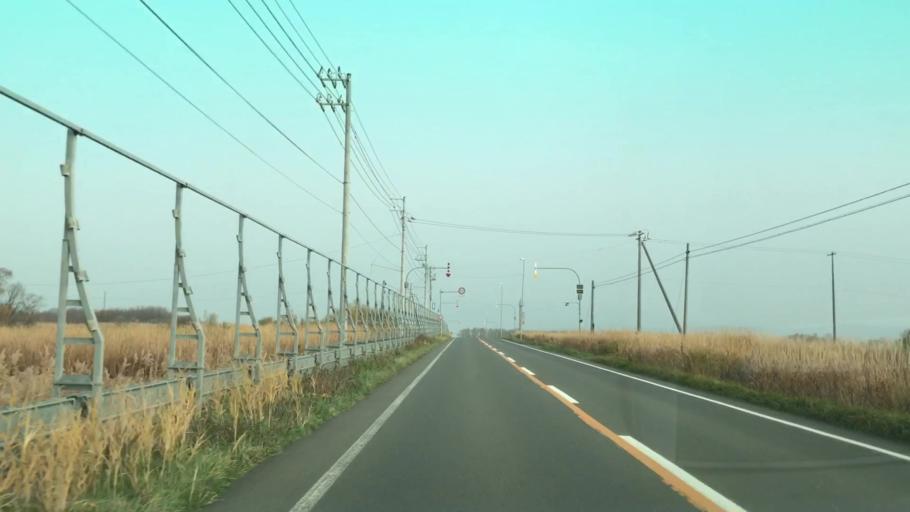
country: JP
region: Hokkaido
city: Ishikari
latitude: 43.2994
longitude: 141.4117
